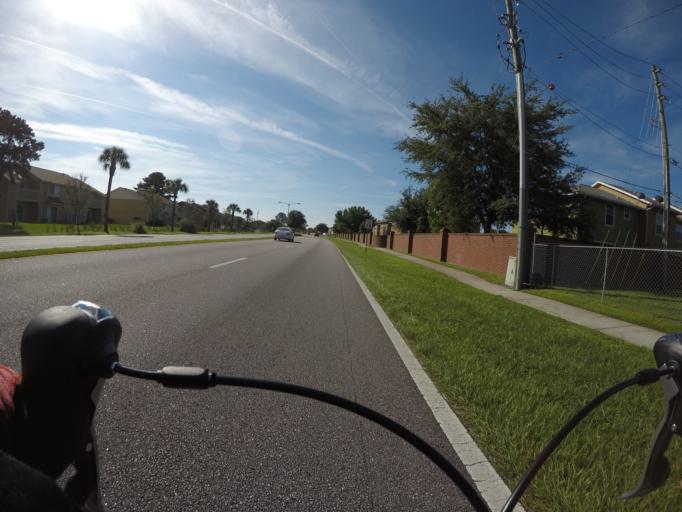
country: US
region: Florida
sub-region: Osceola County
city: Buenaventura Lakes
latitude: 28.3248
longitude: -81.3475
